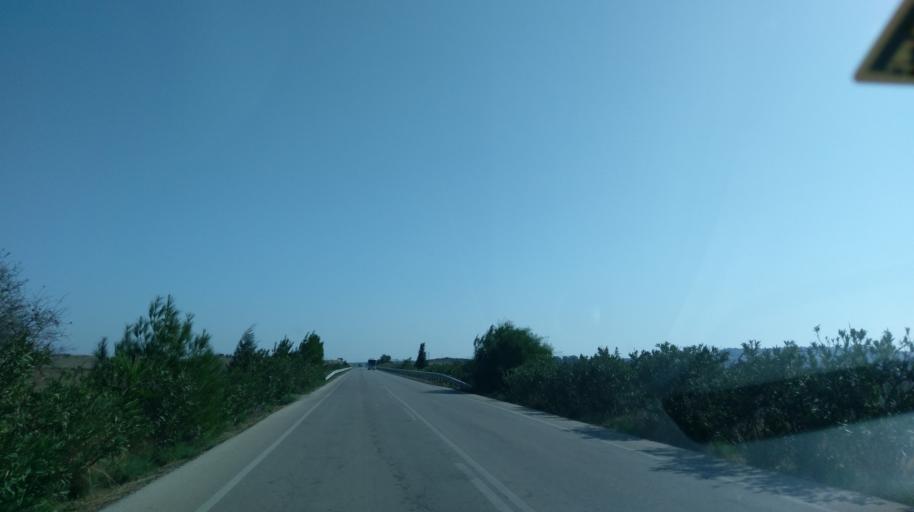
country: CY
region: Ammochostos
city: Leonarisso
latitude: 35.3796
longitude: 34.0225
